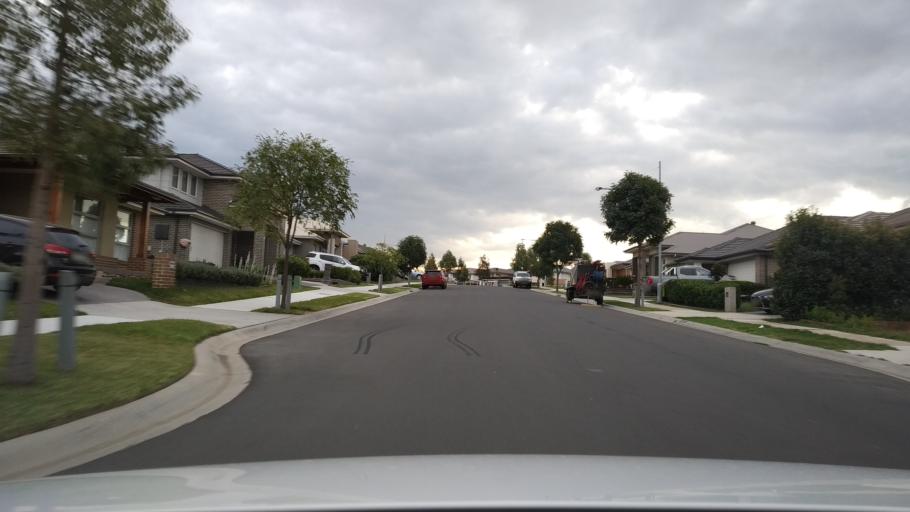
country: AU
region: New South Wales
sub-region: Camden
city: Narellan
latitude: -34.0020
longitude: 150.7321
